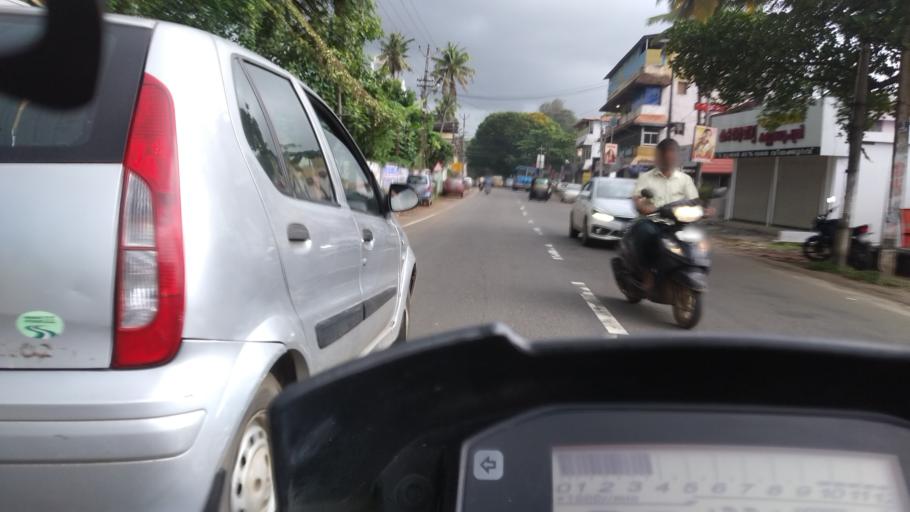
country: IN
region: Kerala
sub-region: Thiruvananthapuram
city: Attingal
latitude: 8.7021
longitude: 76.8140
